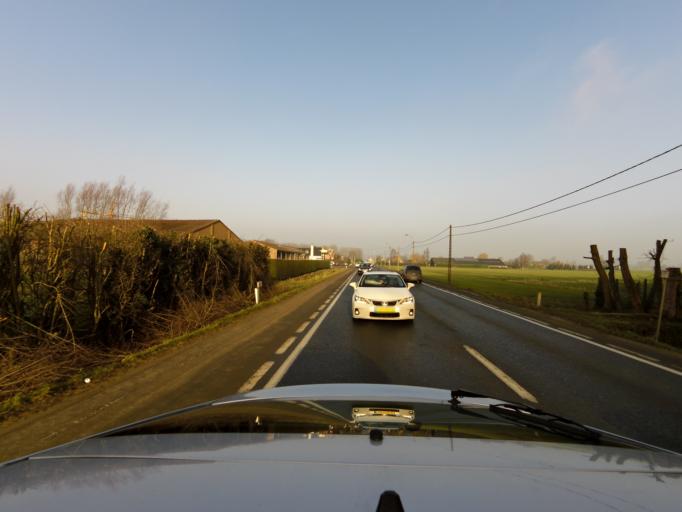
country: BE
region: Flanders
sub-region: Provincie West-Vlaanderen
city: Ichtegem
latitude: 51.1255
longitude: 2.9929
